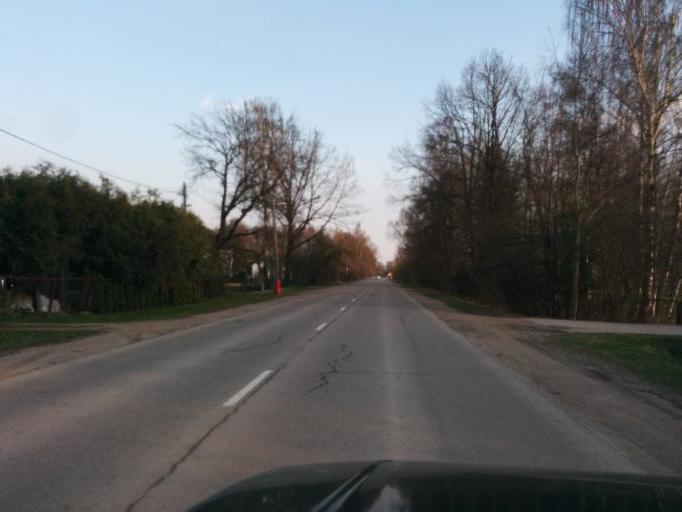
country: LV
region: Jelgava
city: Jelgava
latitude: 56.6638
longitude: 23.7355
